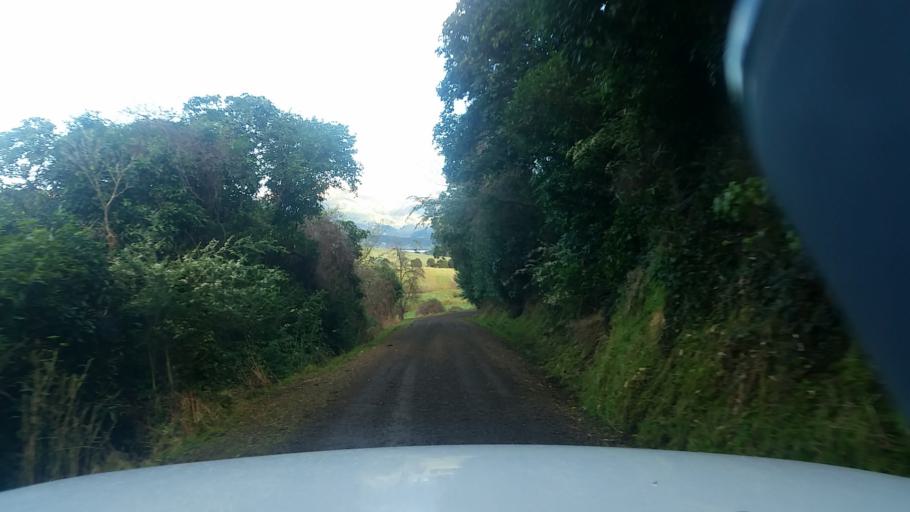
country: NZ
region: Canterbury
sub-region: Christchurch City
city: Christchurch
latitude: -43.7580
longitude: 172.9753
